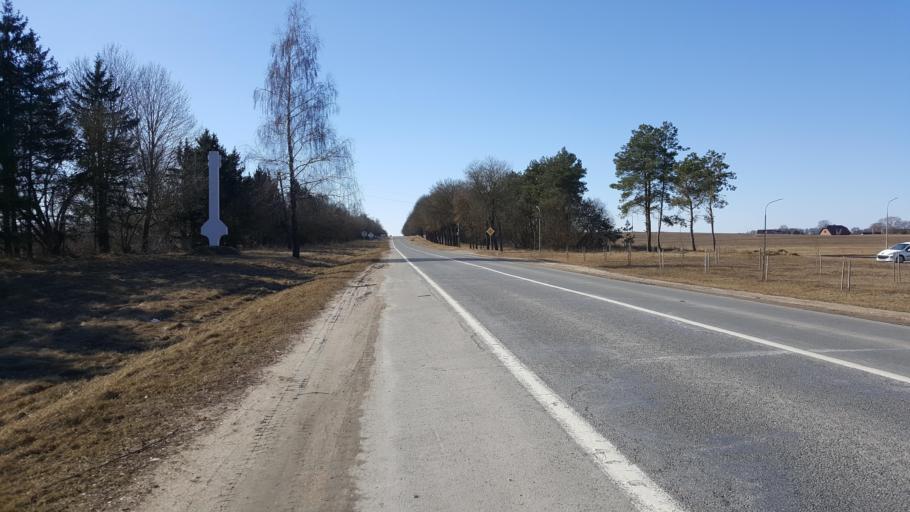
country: BY
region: Brest
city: Kamyanyets
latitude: 52.3880
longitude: 23.8185
